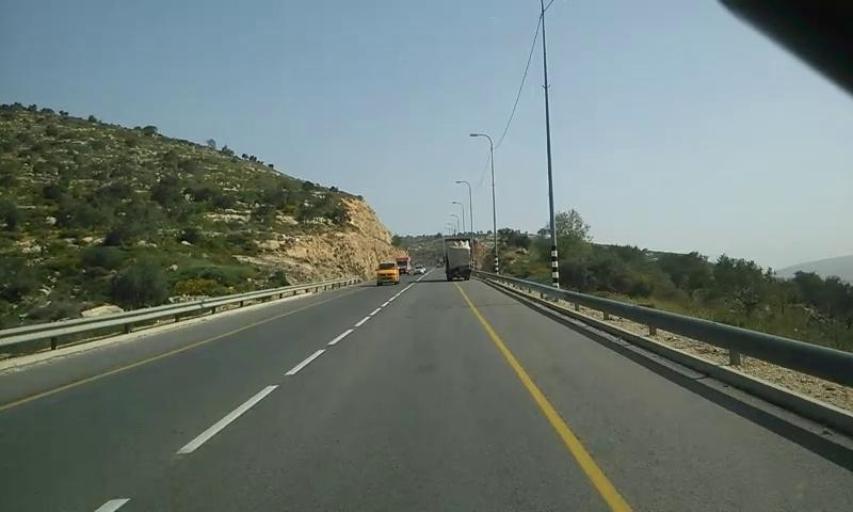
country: PS
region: West Bank
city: Yatma
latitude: 32.1088
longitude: 35.2568
